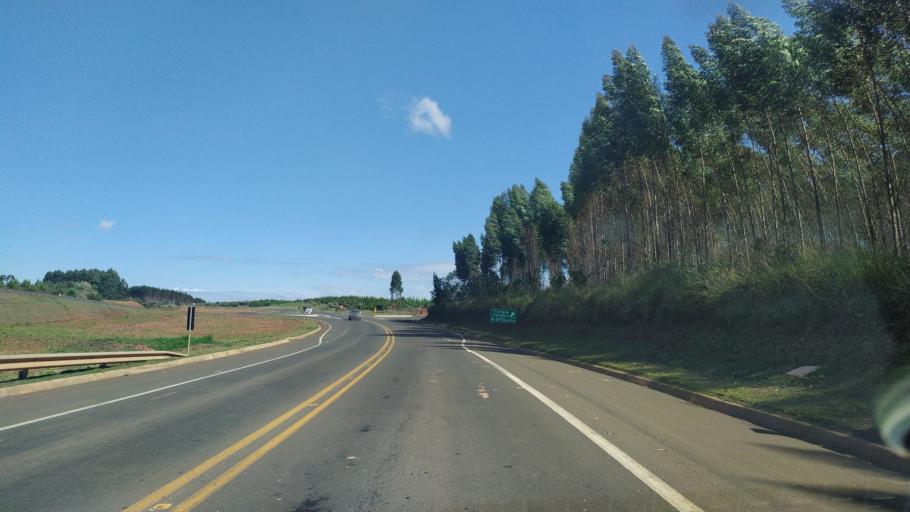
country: BR
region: Parana
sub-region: Telemaco Borba
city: Telemaco Borba
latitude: -24.2444
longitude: -50.7743
